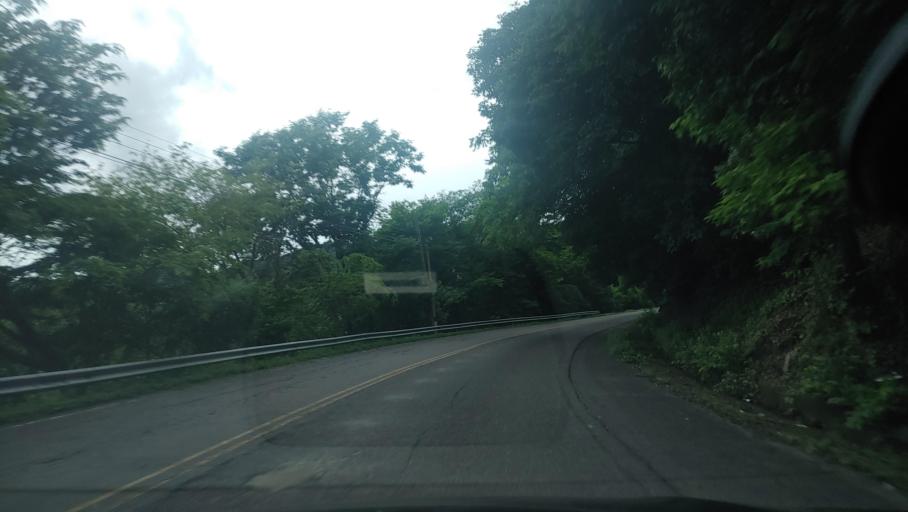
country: HN
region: Choluteca
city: Corpus
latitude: 13.3725
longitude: -87.0418
